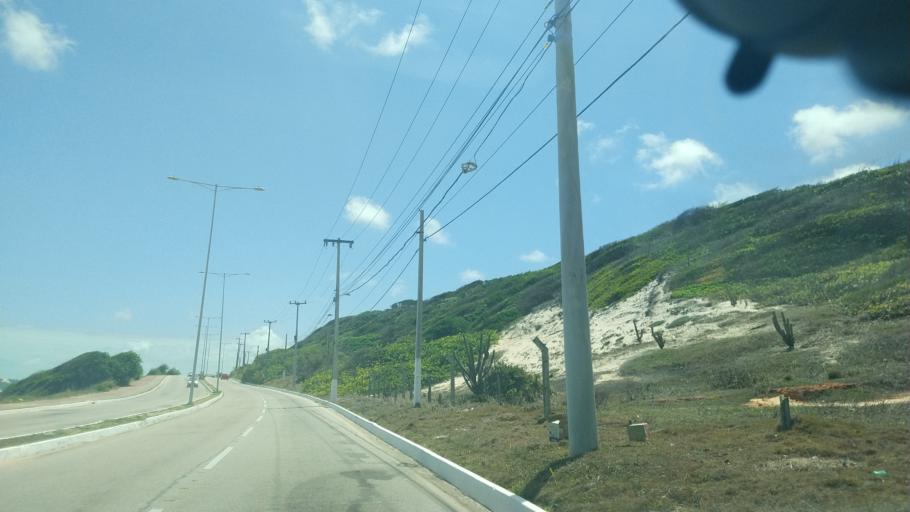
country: BR
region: Rio Grande do Norte
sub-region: Natal
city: Natal
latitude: -5.8373
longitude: -35.1825
